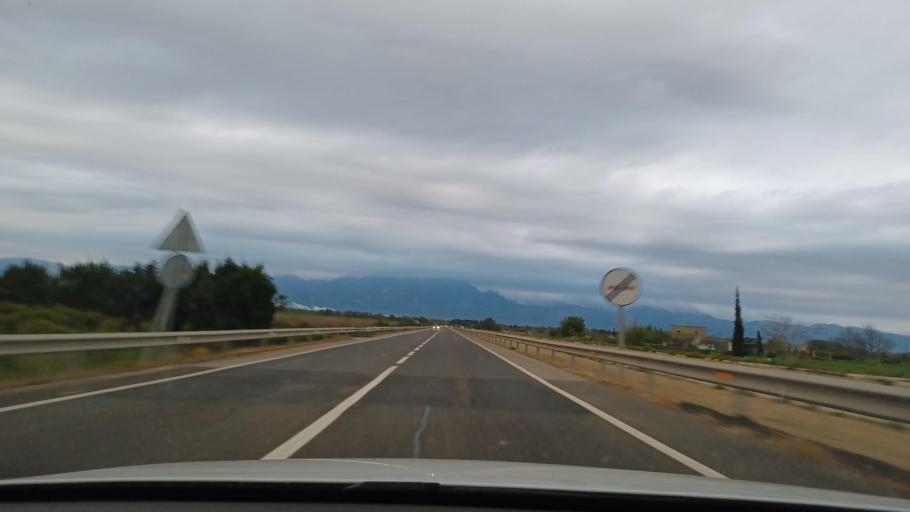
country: ES
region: Catalonia
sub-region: Provincia de Tarragona
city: Masdenverge
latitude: 40.7478
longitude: 0.5564
